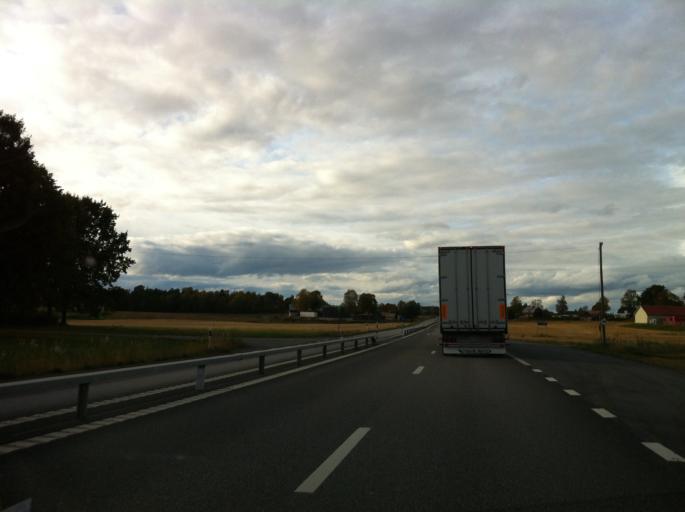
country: SE
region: OErebro
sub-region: Askersunds Kommun
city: Askersund
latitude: 58.7920
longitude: 14.9799
